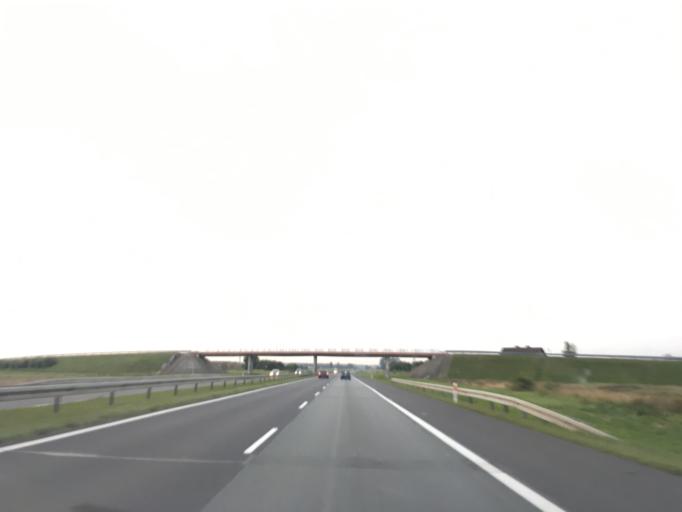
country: PL
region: Lodz Voivodeship
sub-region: Powiat piotrkowski
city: Grabica
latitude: 51.4787
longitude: 19.6246
